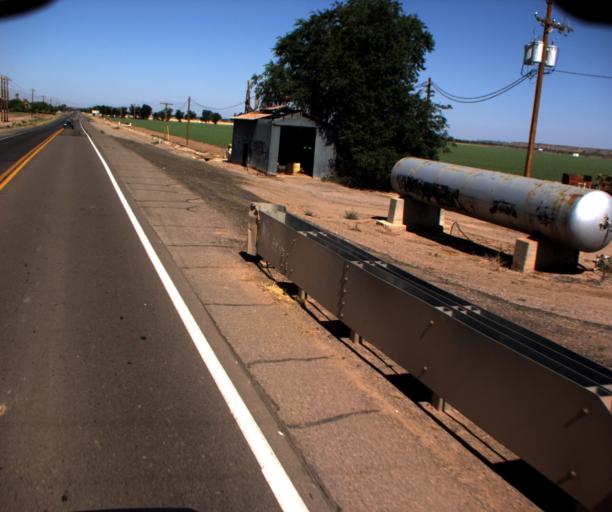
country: US
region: Arizona
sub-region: Graham County
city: Safford
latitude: 32.8166
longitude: -109.6481
